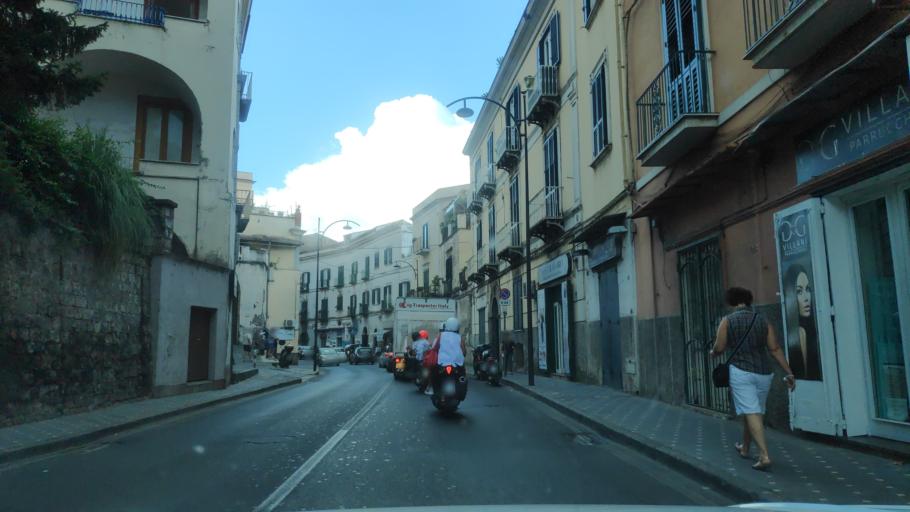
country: IT
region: Campania
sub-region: Provincia di Napoli
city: Meta
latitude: 40.6390
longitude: 14.4187
